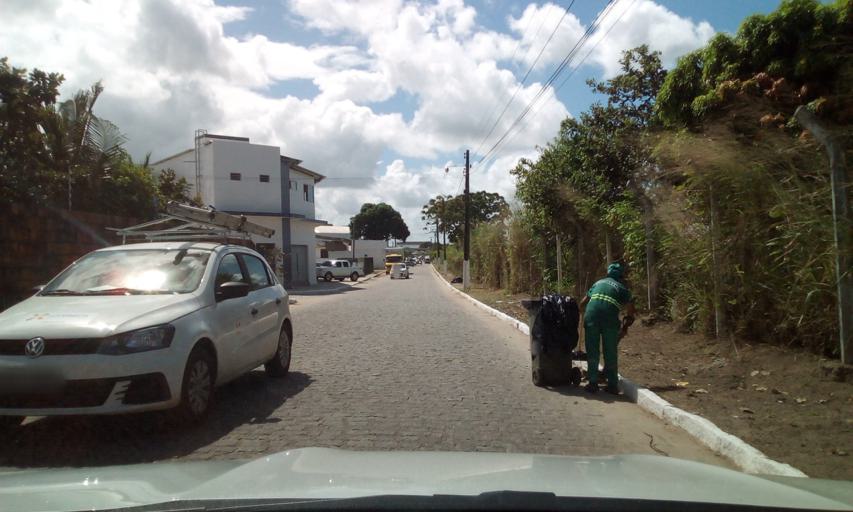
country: BR
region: Paraiba
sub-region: Santa Rita
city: Santa Rita
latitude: -7.1385
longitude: -34.9647
